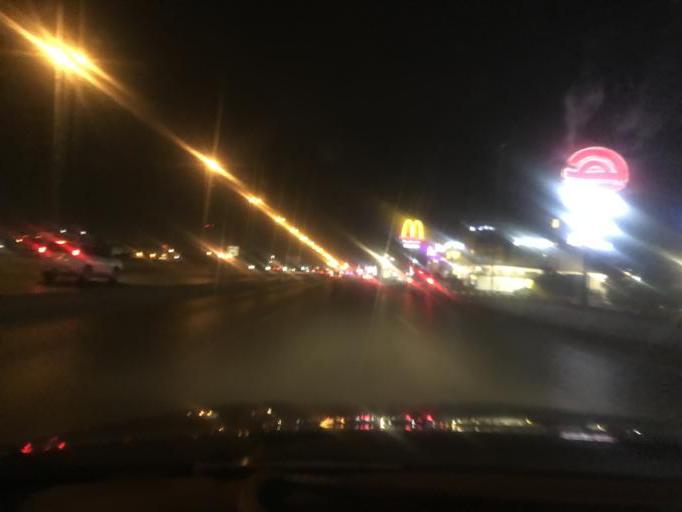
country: SA
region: Ar Riyad
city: Riyadh
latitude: 24.7426
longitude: 46.8075
